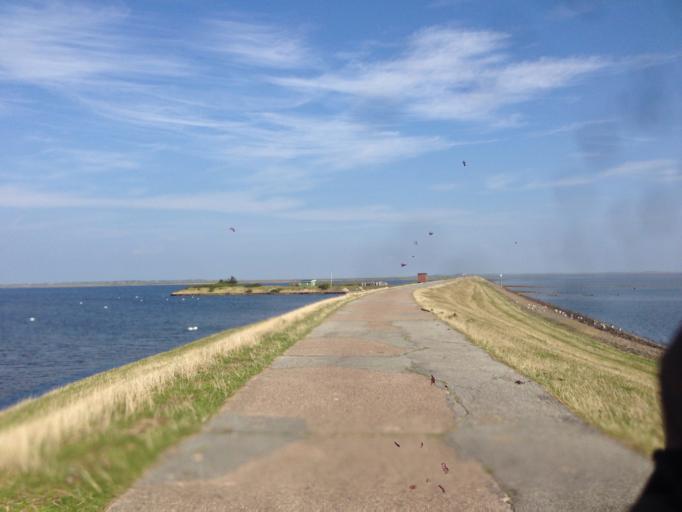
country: DE
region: Schleswig-Holstein
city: Tinnum
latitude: 54.8598
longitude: 8.3089
